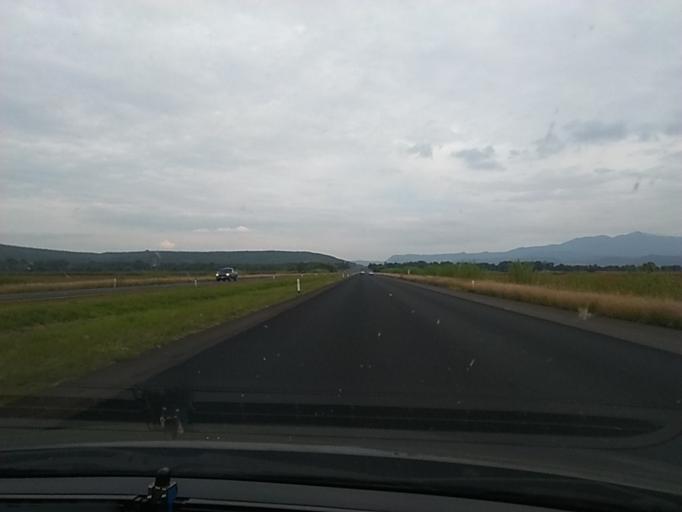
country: MX
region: Michoacan
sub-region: Jimenez
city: Copandaro (Copandaro del Cuatro)
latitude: 19.9090
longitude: -101.5837
